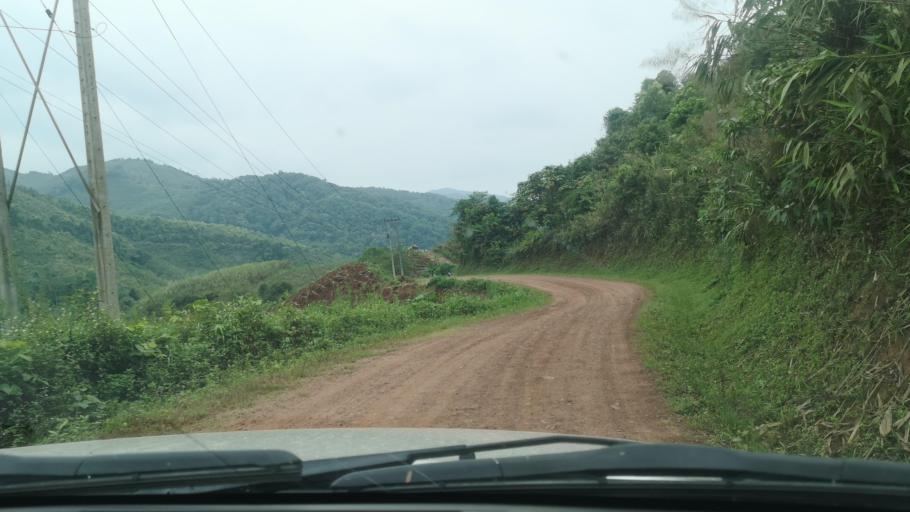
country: LA
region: Oudomxai
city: Muang La
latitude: 21.1687
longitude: 101.8888
